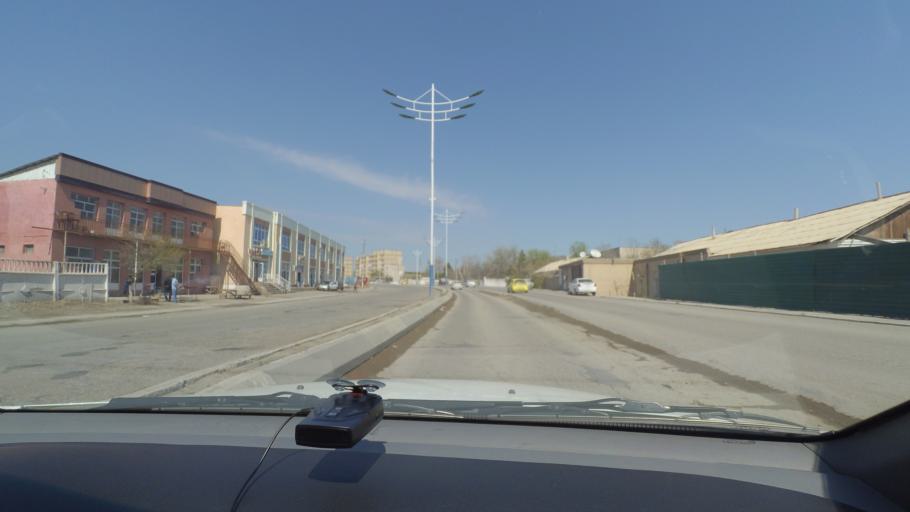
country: UZ
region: Bukhara
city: Bukhara
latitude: 39.7722
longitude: 64.4494
